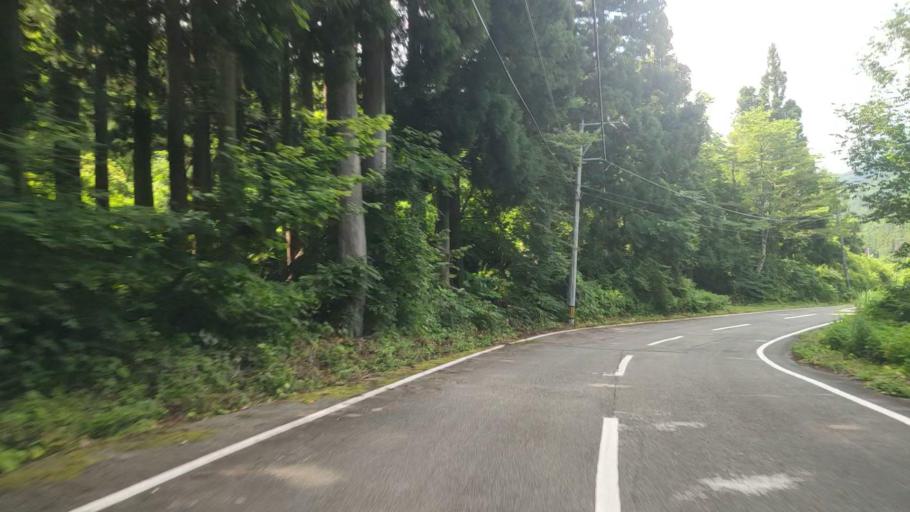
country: JP
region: Fukui
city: Katsuyama
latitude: 36.2137
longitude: 136.5293
